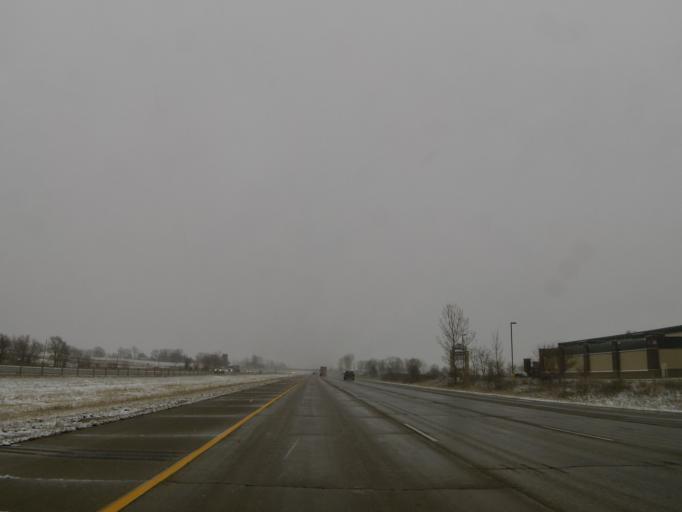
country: US
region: Minnesota
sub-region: Washington County
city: Lake Elmo
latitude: 44.9485
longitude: -92.8952
